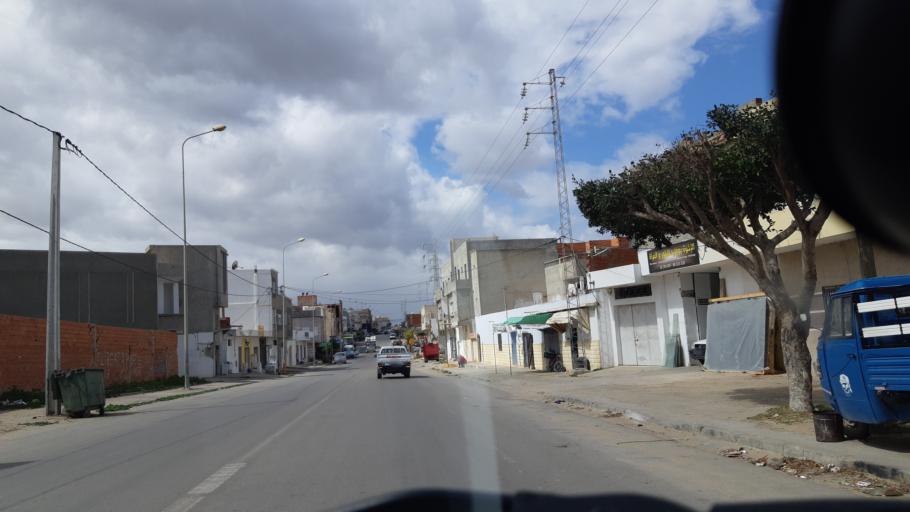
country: TN
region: Susah
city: Akouda
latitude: 35.8790
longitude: 10.5218
